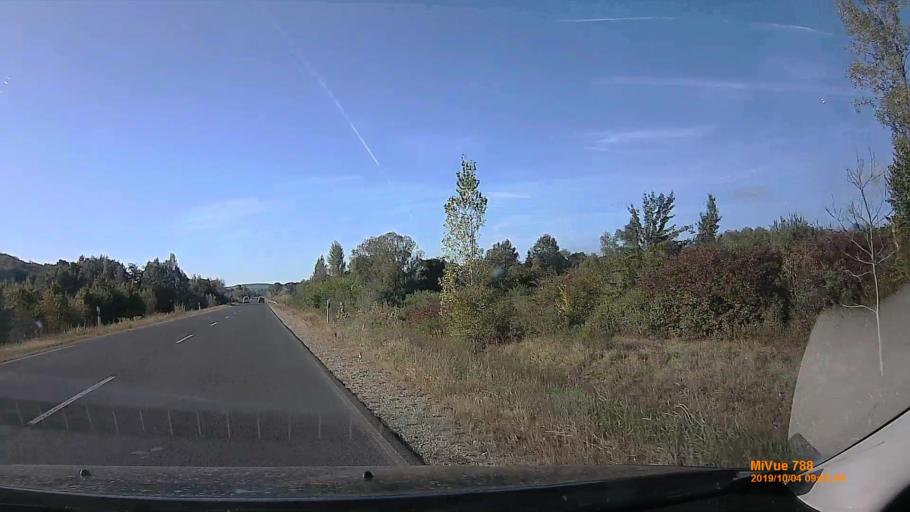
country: HU
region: Somogy
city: Karad
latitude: 46.7207
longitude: 17.7750
